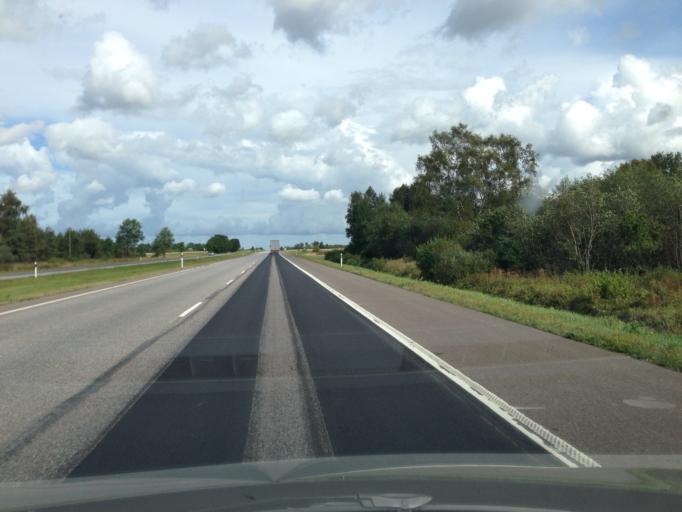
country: EE
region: Harju
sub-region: Saue linn
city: Saue
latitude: 59.2950
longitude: 24.5488
